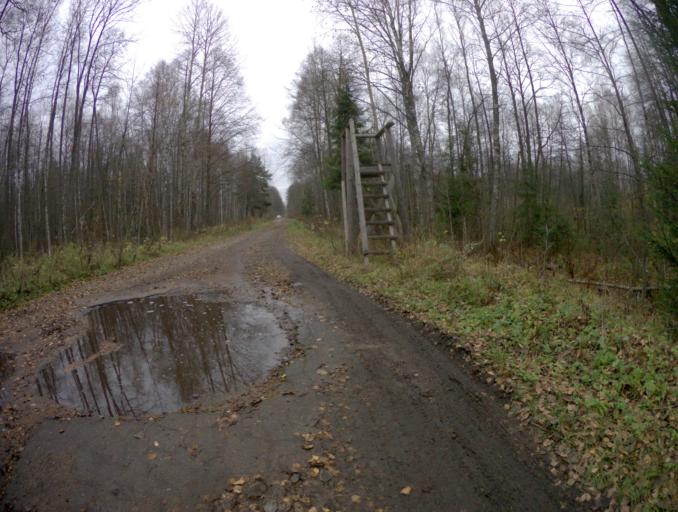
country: RU
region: Vladimir
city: Krasnyy Oktyabr'
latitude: 56.0130
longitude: 38.8437
